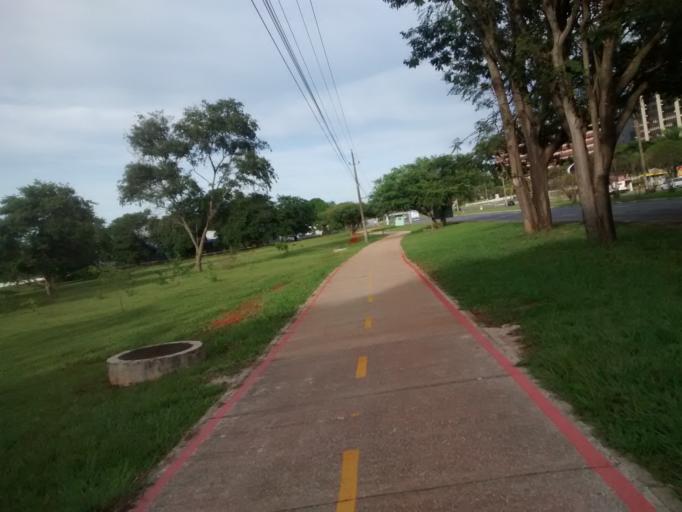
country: BR
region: Federal District
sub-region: Brasilia
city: Brasilia
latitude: -15.8040
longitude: -47.8784
